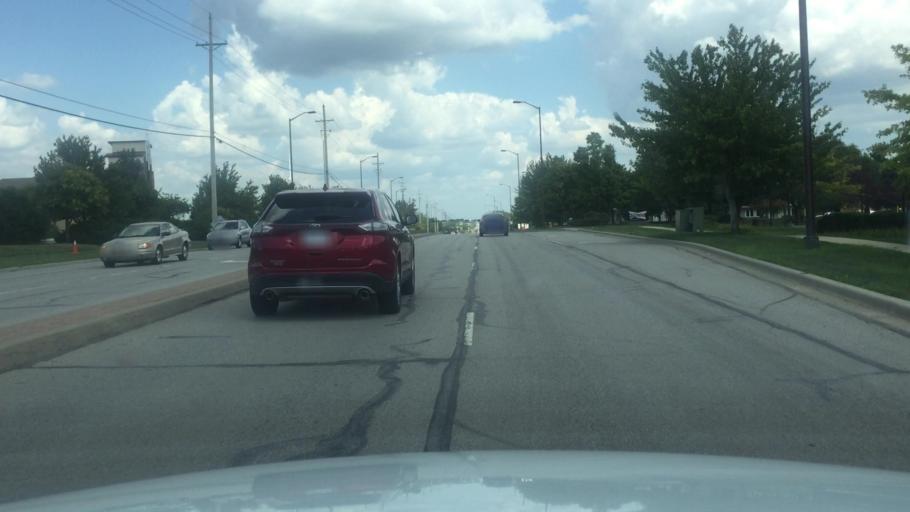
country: US
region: Kansas
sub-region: Johnson County
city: Lenexa
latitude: 38.9710
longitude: -94.7699
